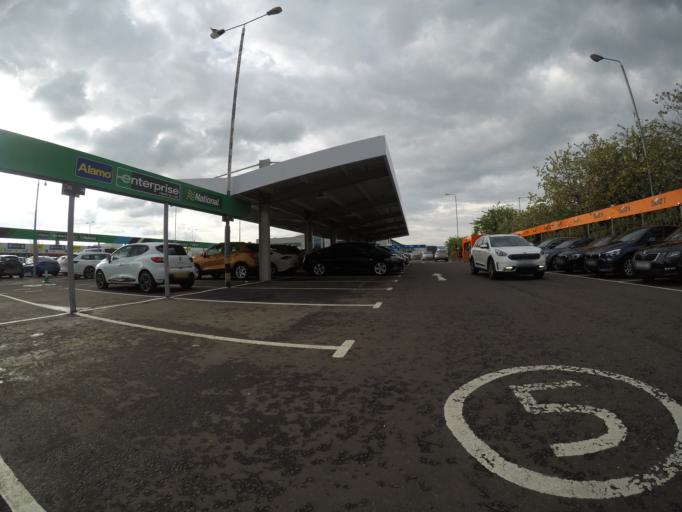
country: GB
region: Scotland
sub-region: Renfrewshire
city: Inchinnan
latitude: 55.8640
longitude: -4.4262
